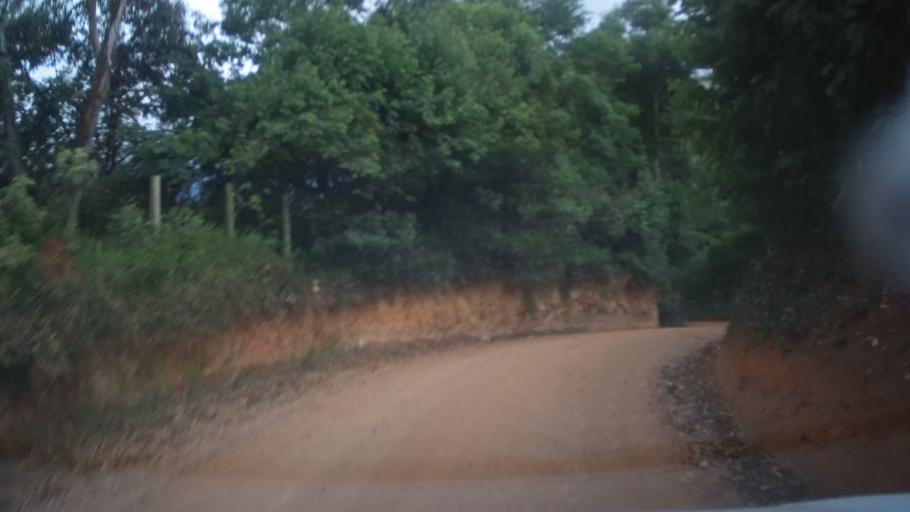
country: BR
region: Sao Paulo
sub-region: Itupeva
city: Itupeva
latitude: -23.1772
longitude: -47.0753
